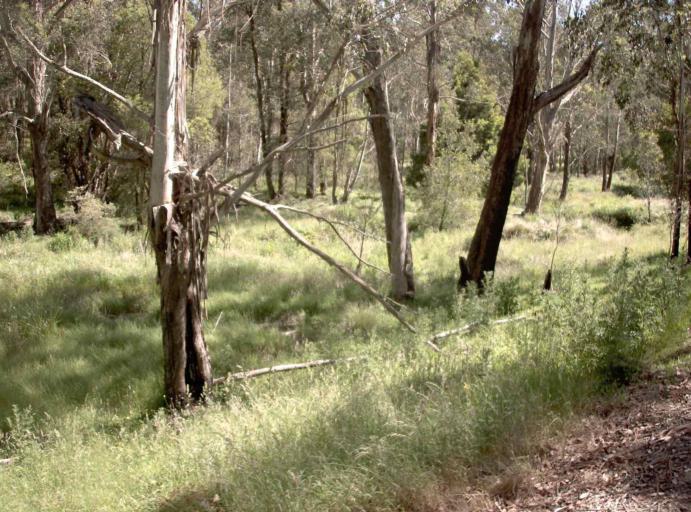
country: AU
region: New South Wales
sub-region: Bombala
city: Bombala
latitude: -37.1570
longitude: 148.7237
